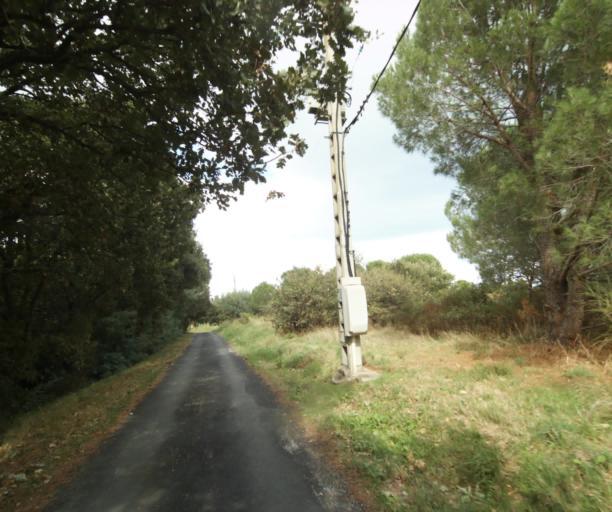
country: FR
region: Languedoc-Roussillon
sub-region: Departement des Pyrenees-Orientales
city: Argelers
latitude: 42.5397
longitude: 3.0185
